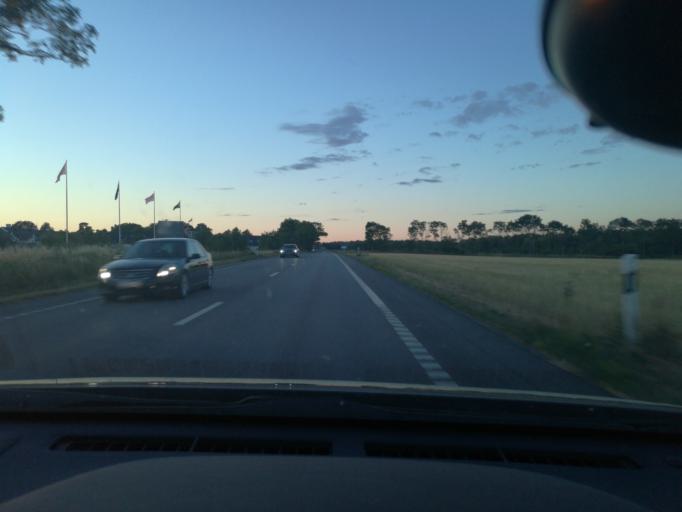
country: SE
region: Kalmar
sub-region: Borgholms Kommun
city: Borgholm
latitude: 56.7818
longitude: 16.5783
